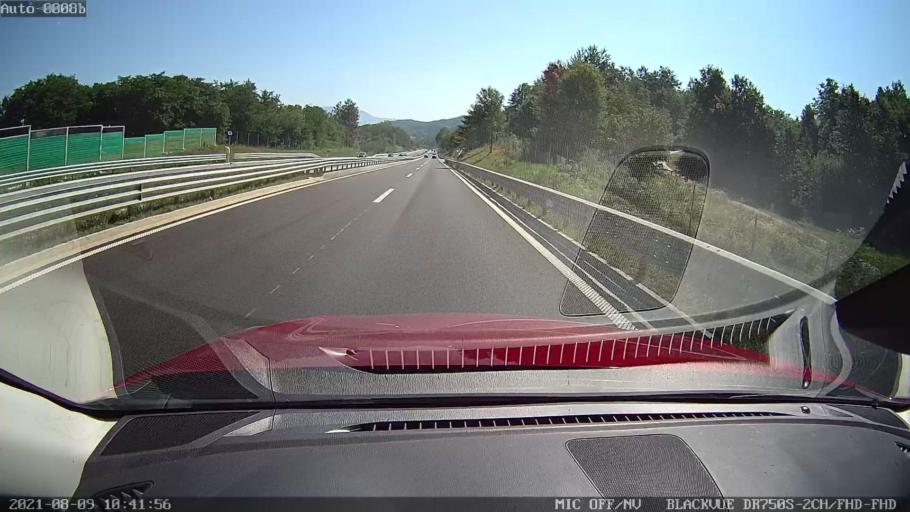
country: HR
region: Istarska
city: Pazin
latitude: 45.2439
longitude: 13.9592
